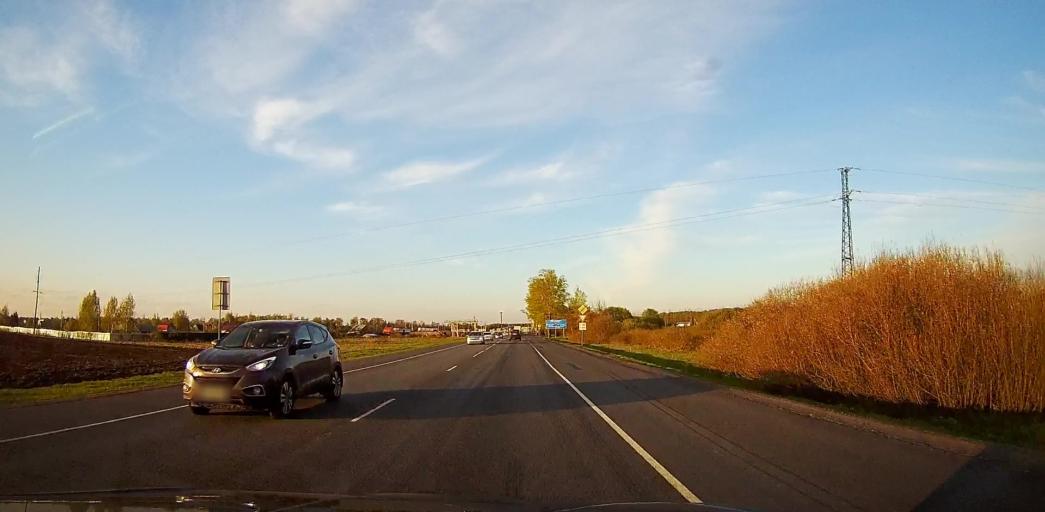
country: RU
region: Moskovskaya
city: Troitskoye
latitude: 55.2750
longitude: 38.4874
